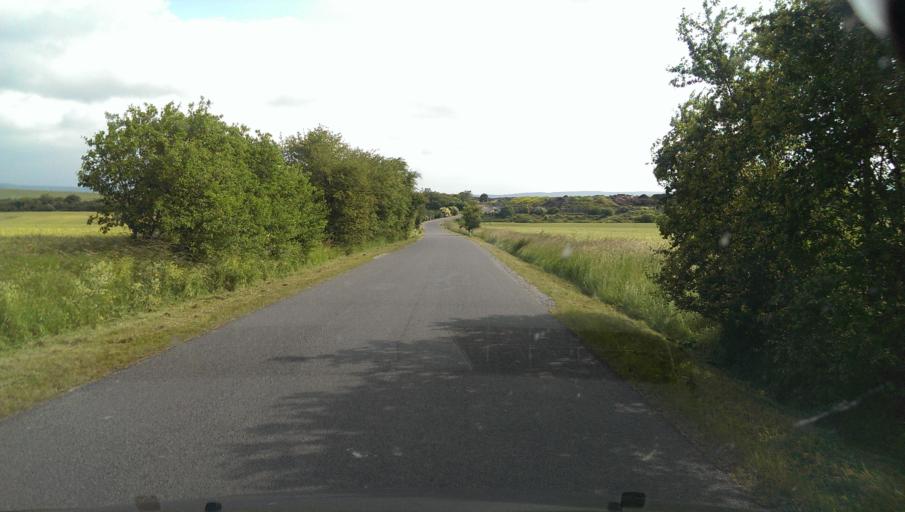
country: DE
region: Thuringia
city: Rittersdorf
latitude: 50.8353
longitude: 11.2414
